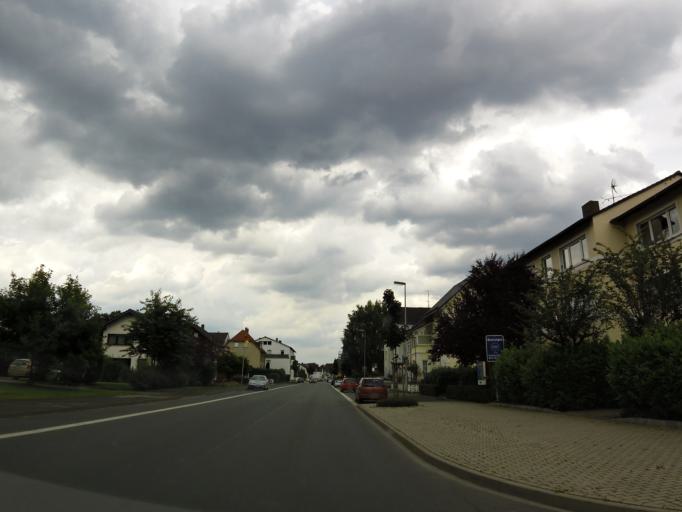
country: DE
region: North Rhine-Westphalia
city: Beverungen
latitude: 51.6587
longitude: 9.3717
